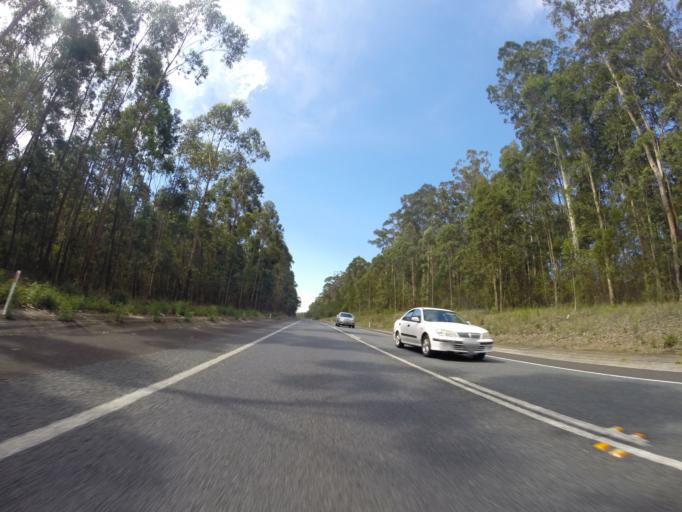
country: AU
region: New South Wales
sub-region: Shoalhaven Shire
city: Falls Creek
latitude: -35.0582
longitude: 150.5752
